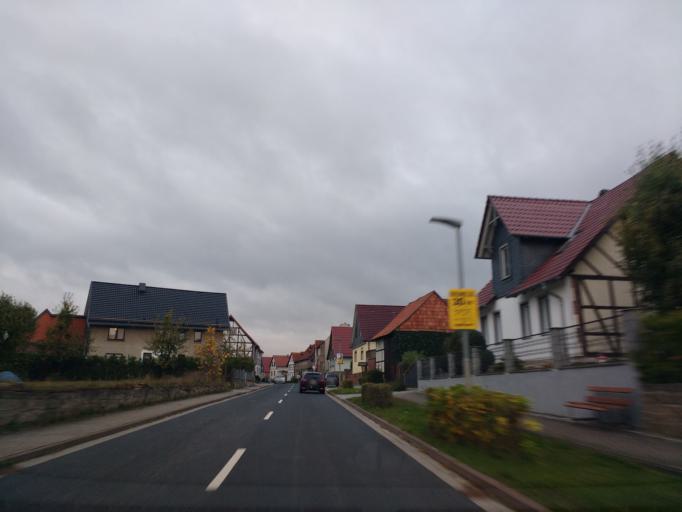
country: DE
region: Thuringia
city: Buhla
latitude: 51.4476
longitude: 10.4477
